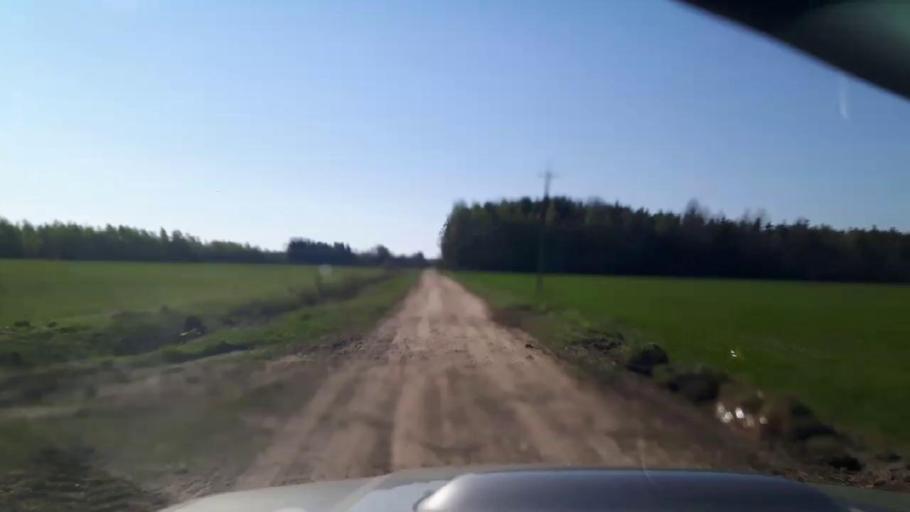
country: EE
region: Paernumaa
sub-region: Tootsi vald
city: Tootsi
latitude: 58.5094
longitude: 24.9342
